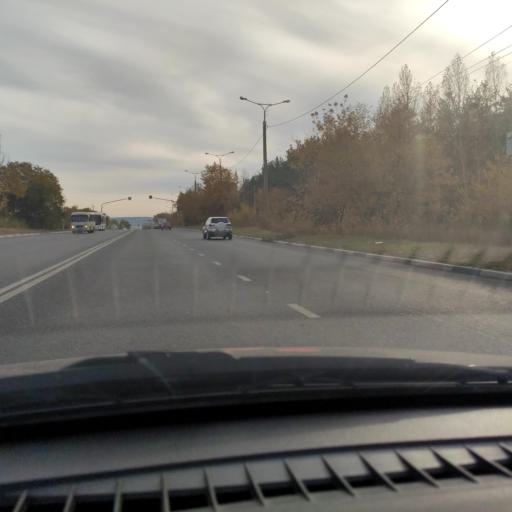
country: RU
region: Samara
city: Zhigulevsk
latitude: 53.4915
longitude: 49.4742
